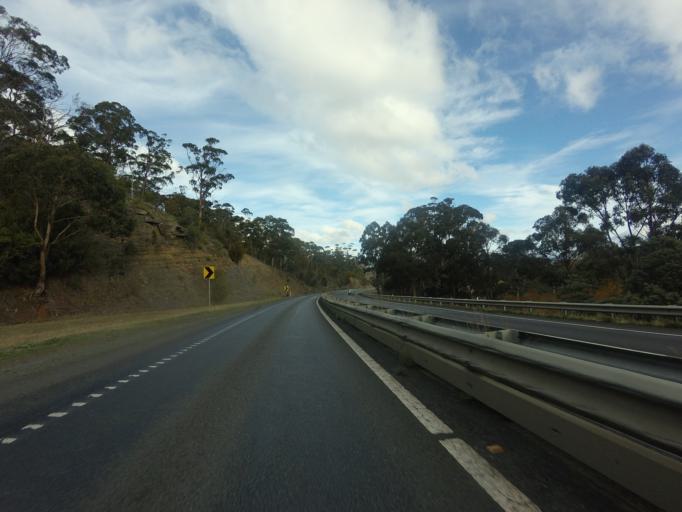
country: AU
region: Tasmania
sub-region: Brighton
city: Bridgewater
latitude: -42.5792
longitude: 147.2285
